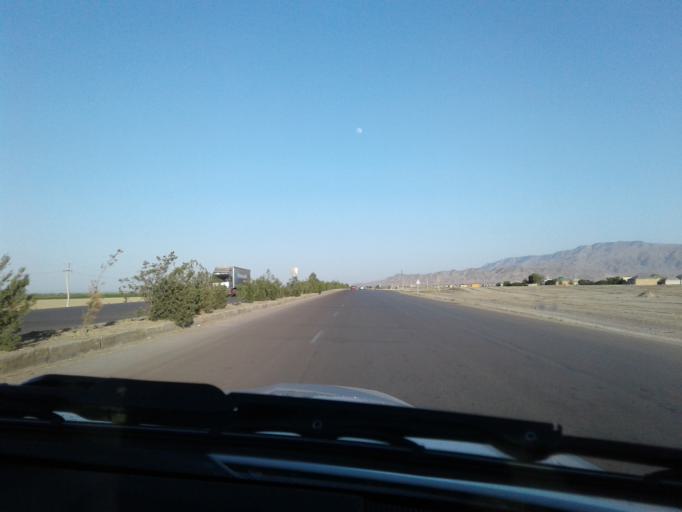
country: TM
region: Ahal
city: Baharly
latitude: 38.3161
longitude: 57.6038
